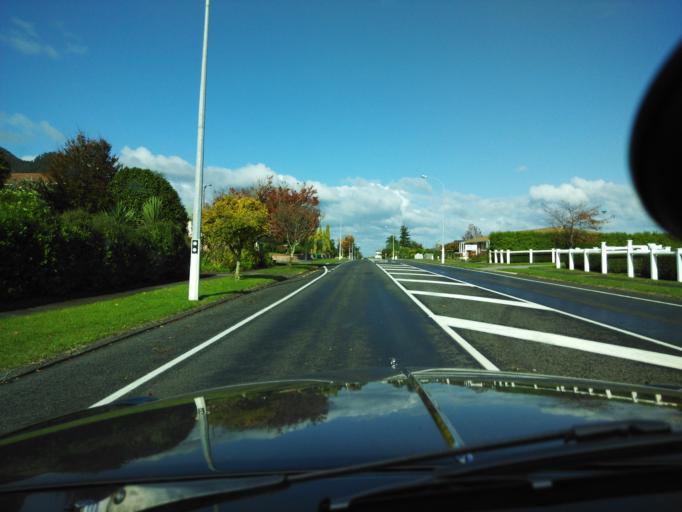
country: NZ
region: Waikato
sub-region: Hauraki District
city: Paeroa
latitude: -37.5275
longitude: 175.7053
